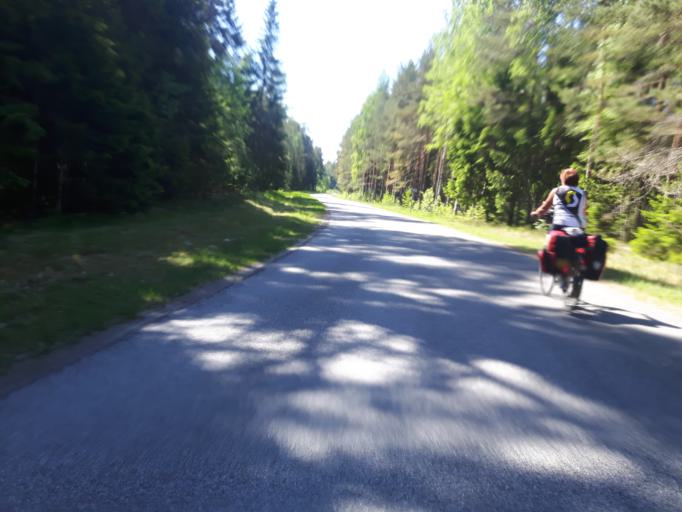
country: EE
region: Laeaene-Virumaa
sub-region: Haljala vald
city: Haljala
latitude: 59.5533
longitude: 26.3455
